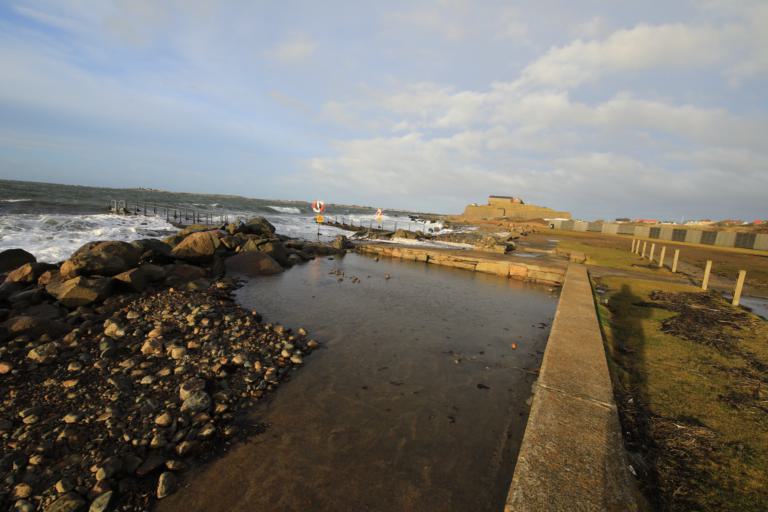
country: SE
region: Halland
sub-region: Varbergs Kommun
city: Varberg
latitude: 57.1004
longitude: 12.2415
